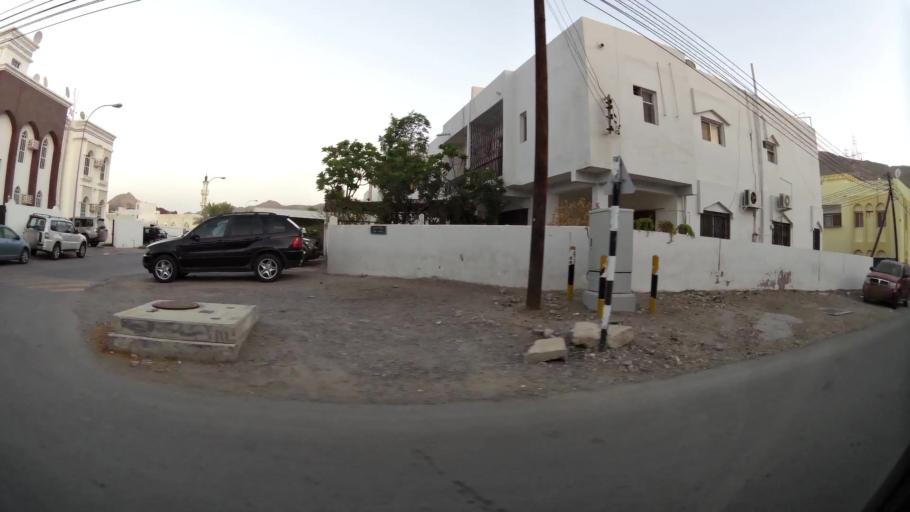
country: OM
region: Muhafazat Masqat
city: Muscat
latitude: 23.5843
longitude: 58.5627
